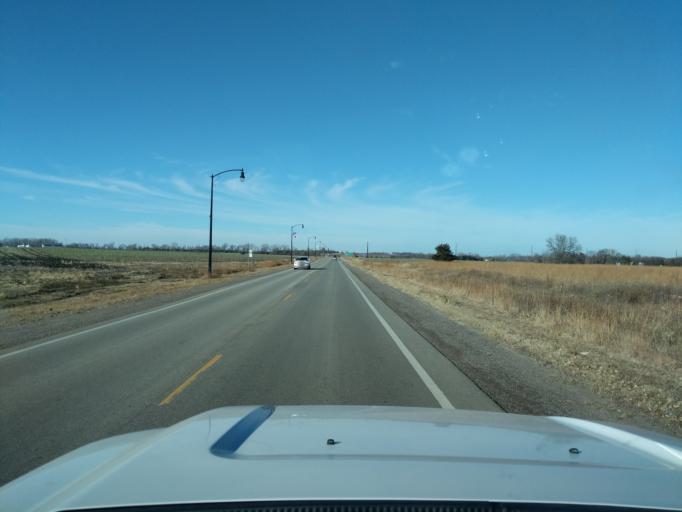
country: US
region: Minnesota
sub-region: Yellow Medicine County
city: Granite Falls
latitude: 44.7676
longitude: -95.5373
